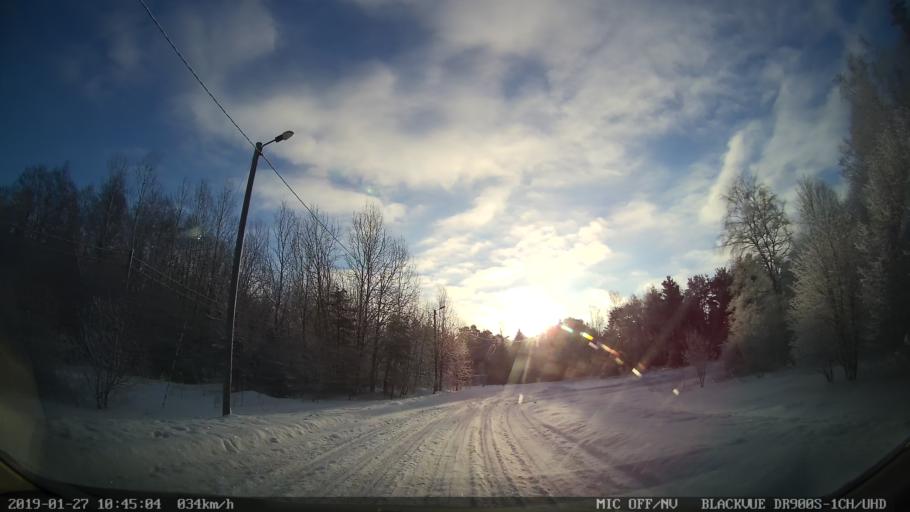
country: EE
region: Harju
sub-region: Kuusalu vald
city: Kuusalu
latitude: 59.5004
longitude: 25.3071
